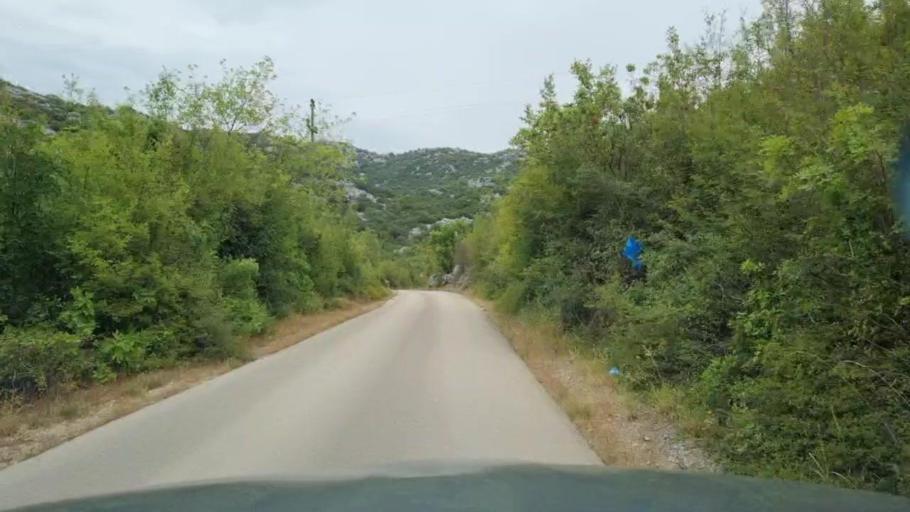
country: BA
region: Federation of Bosnia and Herzegovina
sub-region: Hercegovacko-Bosanski Kanton
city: Neum
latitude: 42.9254
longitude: 17.6817
